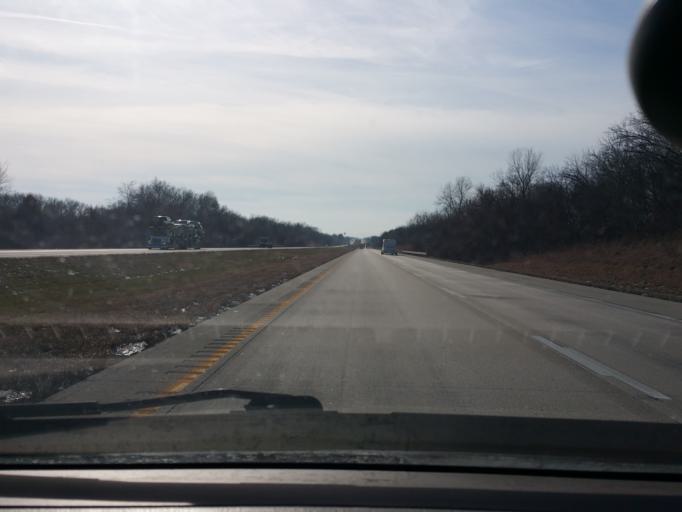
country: US
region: Missouri
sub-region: Clay County
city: Kearney
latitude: 39.3976
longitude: -94.3564
